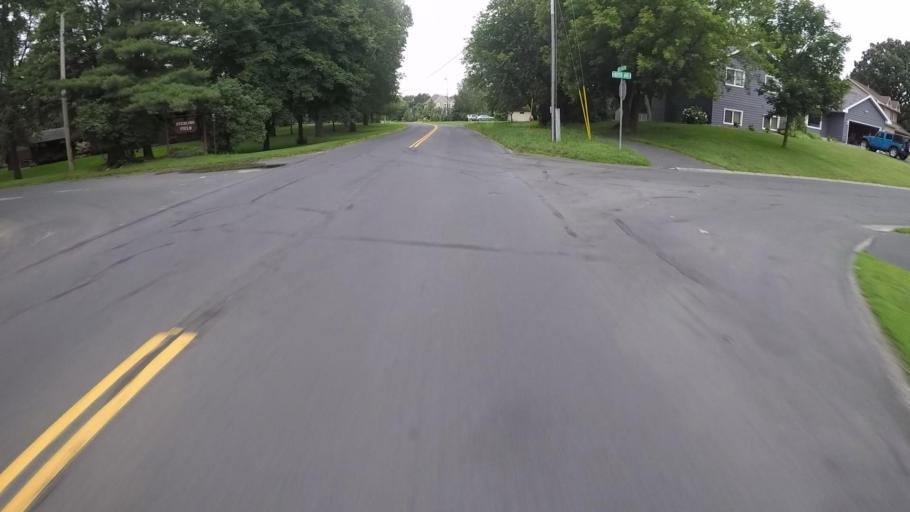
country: US
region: Minnesota
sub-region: Hennepin County
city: Minnetonka
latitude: 44.8804
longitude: -93.4975
